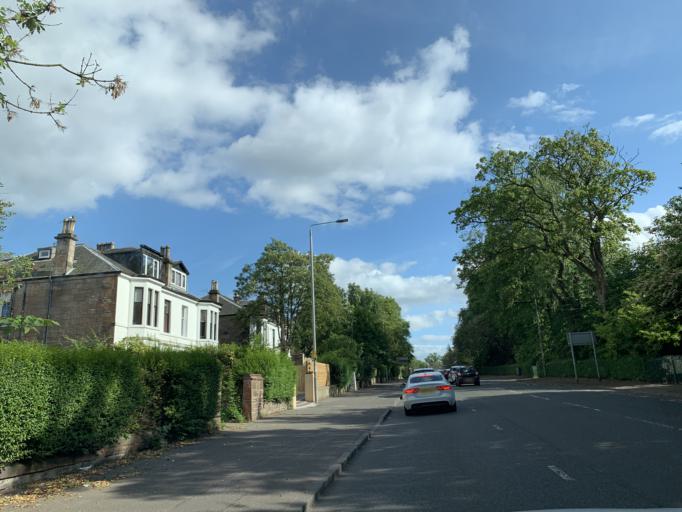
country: GB
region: Scotland
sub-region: East Renfrewshire
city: Giffnock
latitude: 55.8461
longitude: -4.3100
